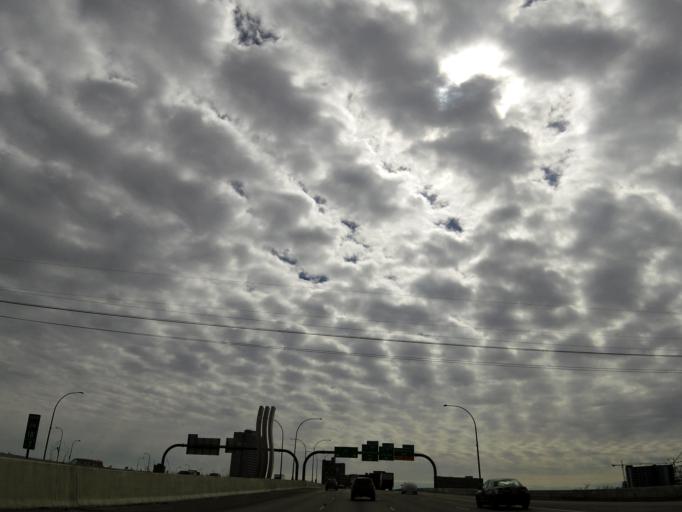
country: US
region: Minnesota
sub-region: Hennepin County
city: Minneapolis
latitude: 44.9813
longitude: -93.2443
